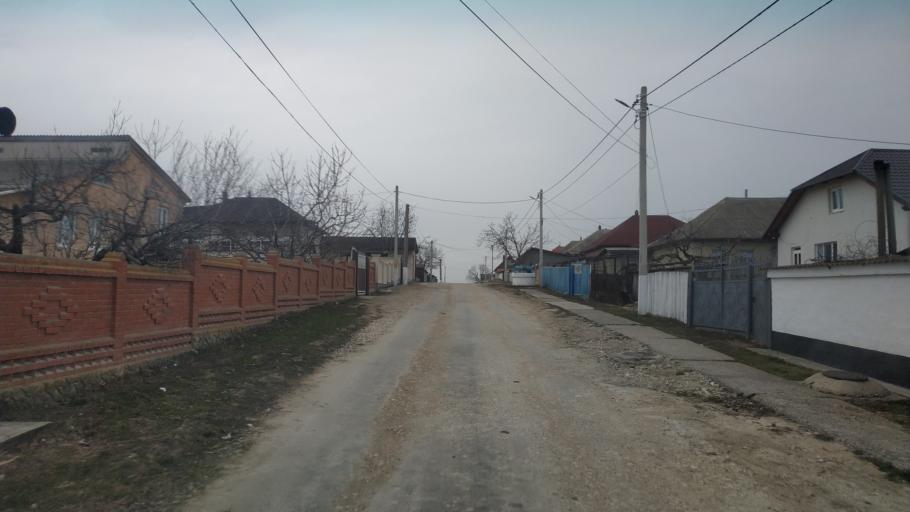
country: MD
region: Chisinau
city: Singera
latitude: 46.8243
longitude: 28.9644
